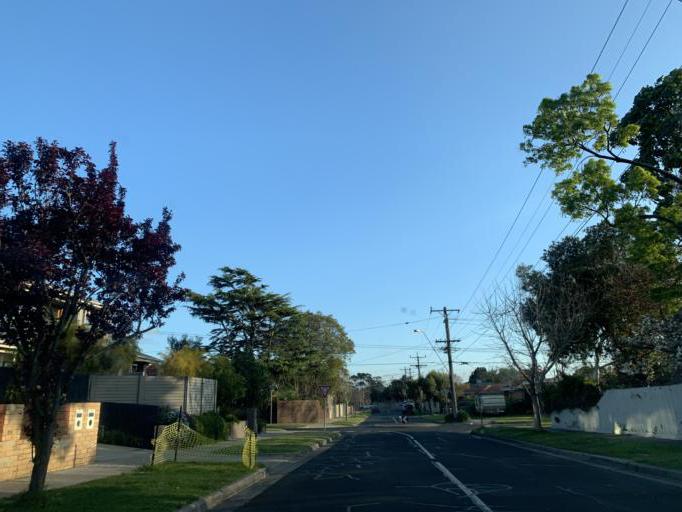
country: AU
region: Victoria
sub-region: Kingston
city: Parkdale
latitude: -37.9821
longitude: 145.0847
